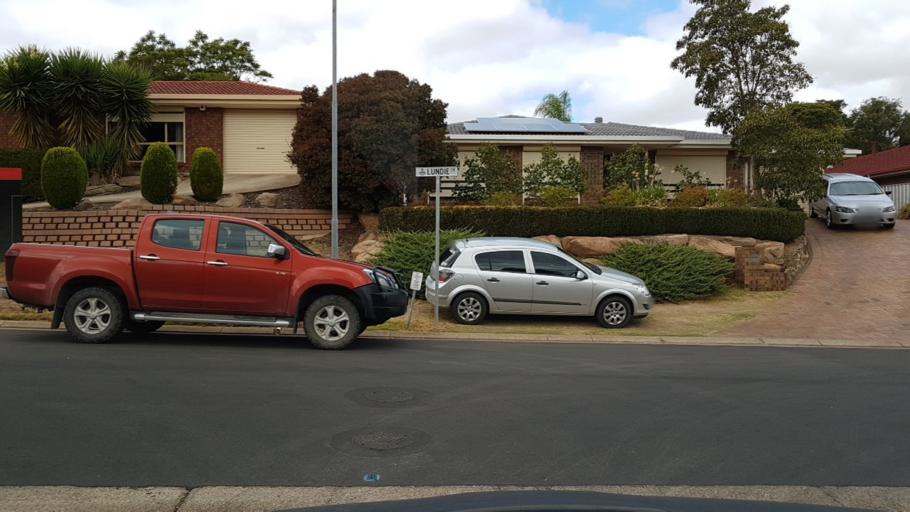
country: AU
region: South Australia
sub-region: Gawler
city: Gawler
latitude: -34.6069
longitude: 138.7586
